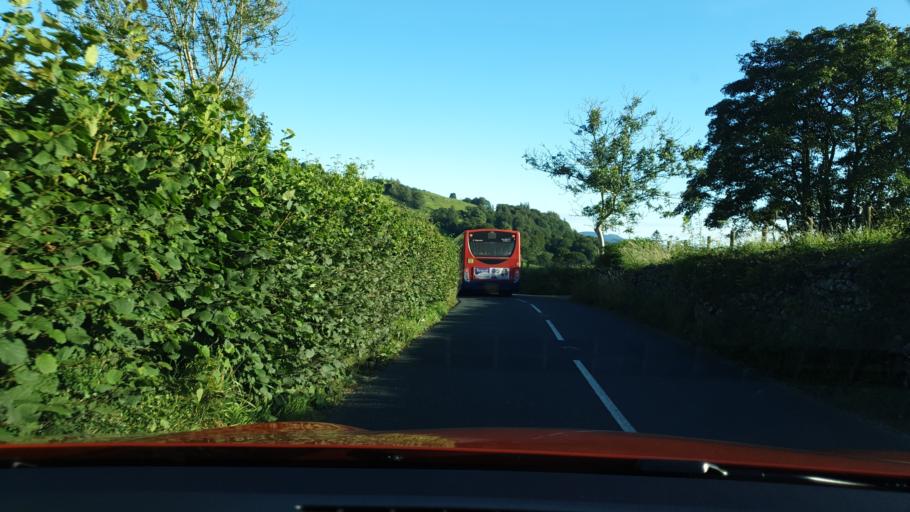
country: GB
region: England
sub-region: Cumbria
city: Windermere
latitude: 54.4232
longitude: -2.9059
